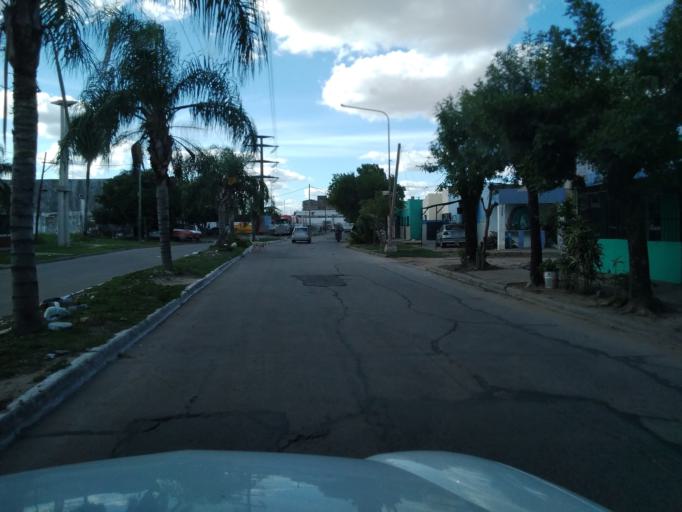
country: AR
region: Corrientes
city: Corrientes
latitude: -27.4868
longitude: -58.8380
